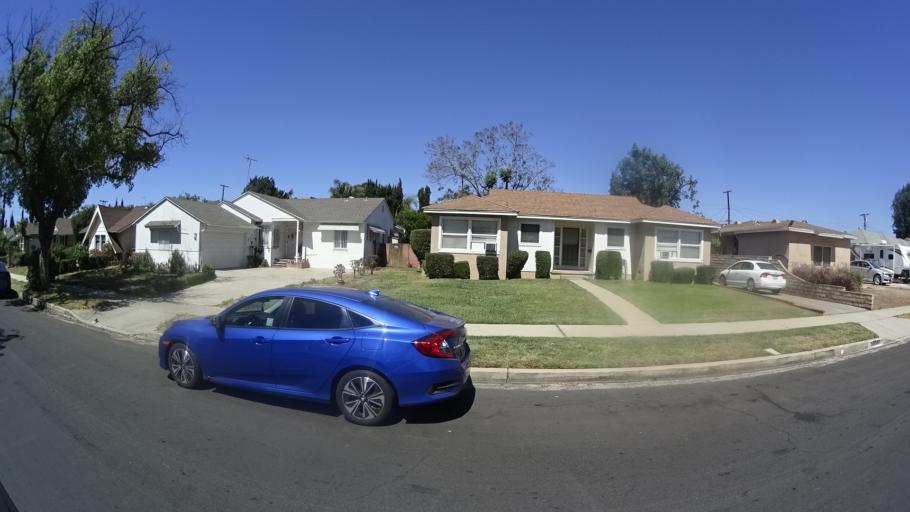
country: US
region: California
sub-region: Los Angeles County
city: San Fernando
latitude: 34.2521
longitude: -118.4630
